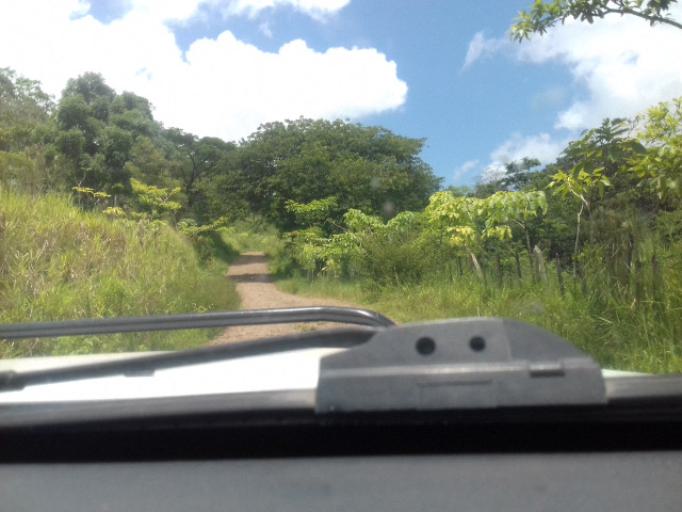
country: NI
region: Matagalpa
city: Matiguas
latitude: 13.0105
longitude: -85.3969
